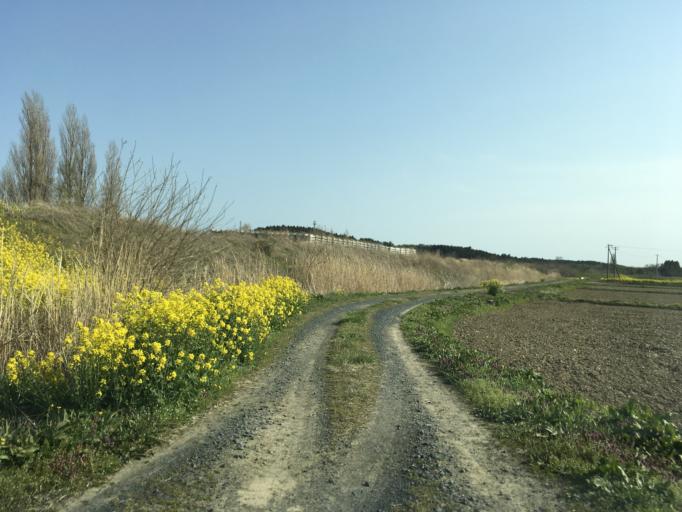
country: JP
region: Miyagi
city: Wakuya
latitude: 38.7155
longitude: 141.2784
